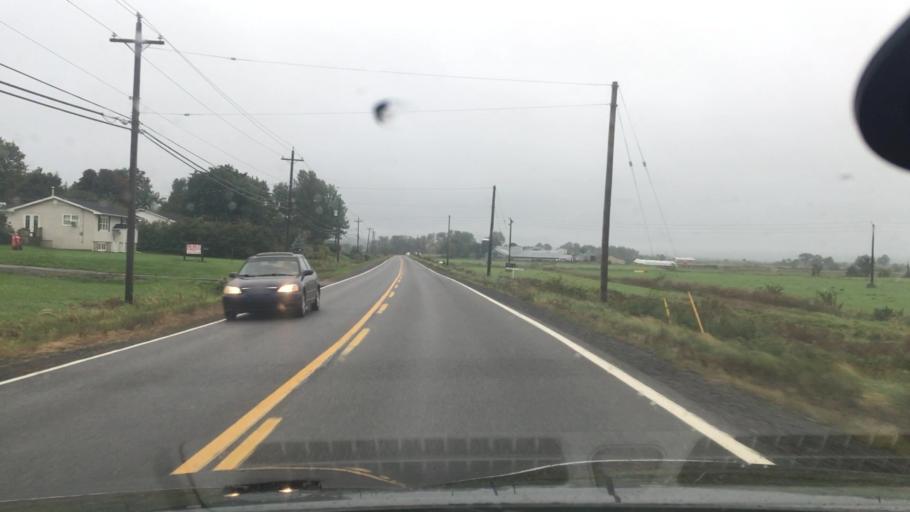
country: CA
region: Nova Scotia
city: Windsor
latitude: 44.9742
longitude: -64.1370
